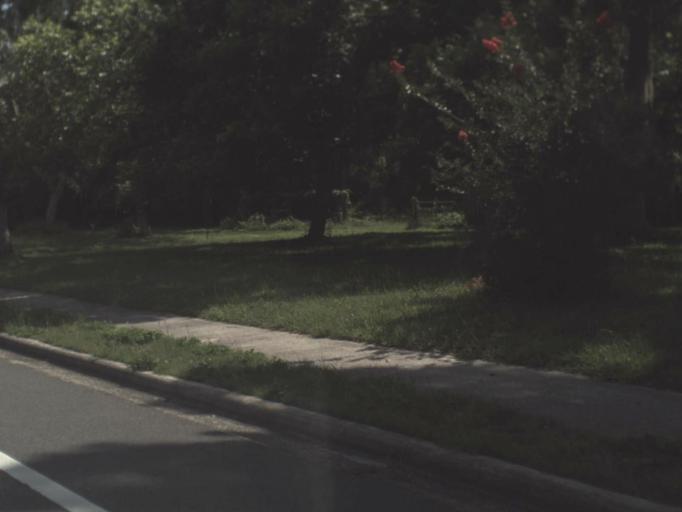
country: US
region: Florida
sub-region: Alachua County
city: Waldo
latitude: 29.7852
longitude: -82.1676
